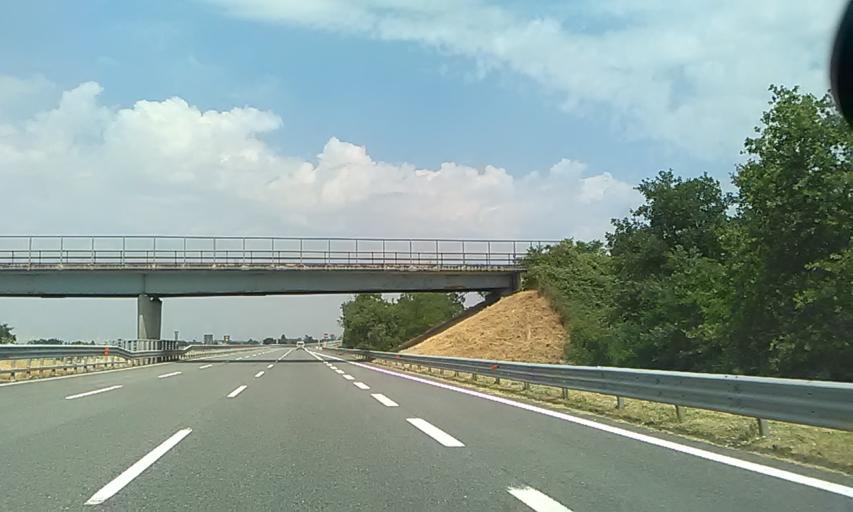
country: IT
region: Piedmont
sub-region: Provincia di Alessandria
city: Castelspina
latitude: 44.8227
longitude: 8.5941
